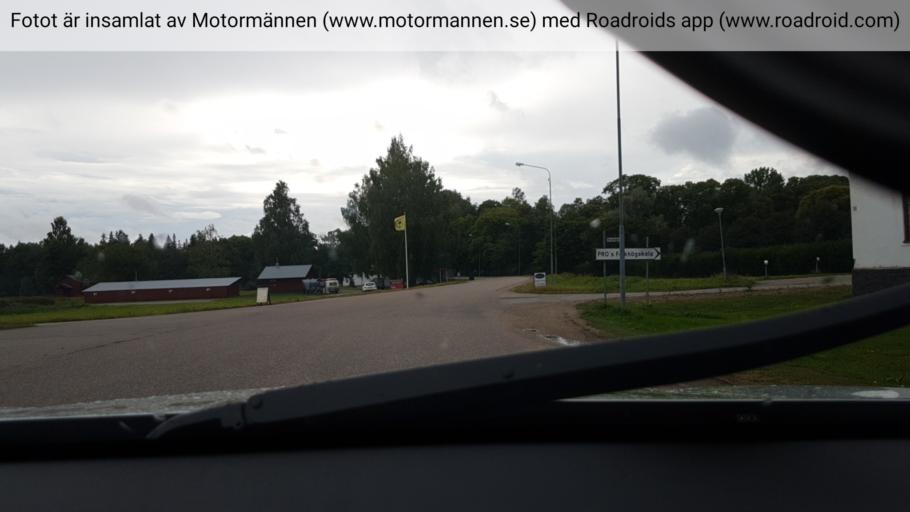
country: SE
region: Uppsala
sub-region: Heby Kommun
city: Tarnsjo
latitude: 60.2895
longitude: 16.8858
